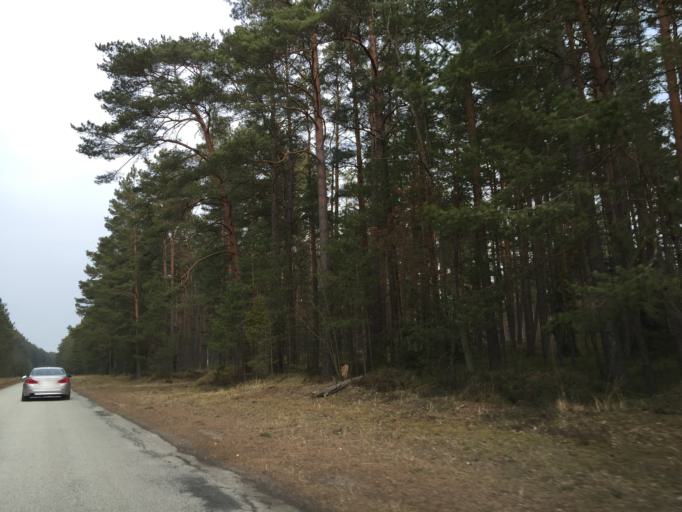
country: LV
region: Salacgrivas
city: Ainazi
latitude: 57.9401
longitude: 24.3920
